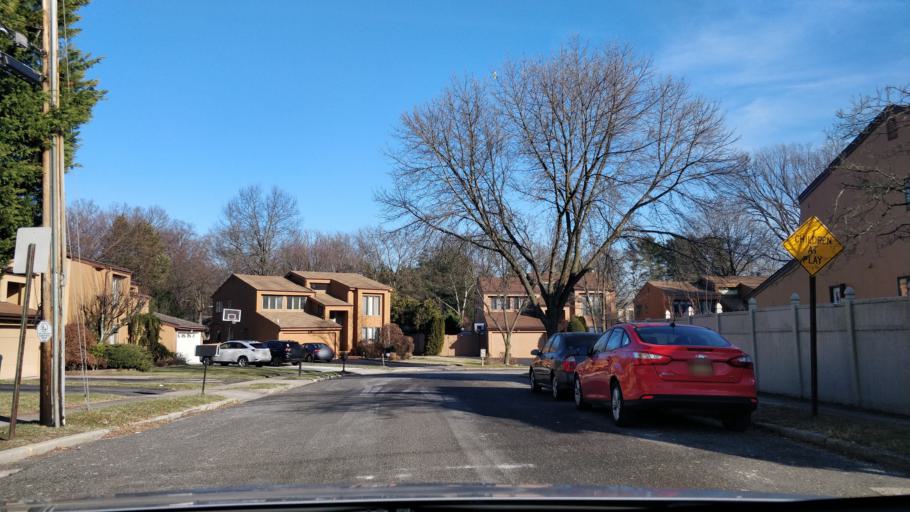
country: US
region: New York
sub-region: Nassau County
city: Greenvale
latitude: 40.8125
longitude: -73.6251
